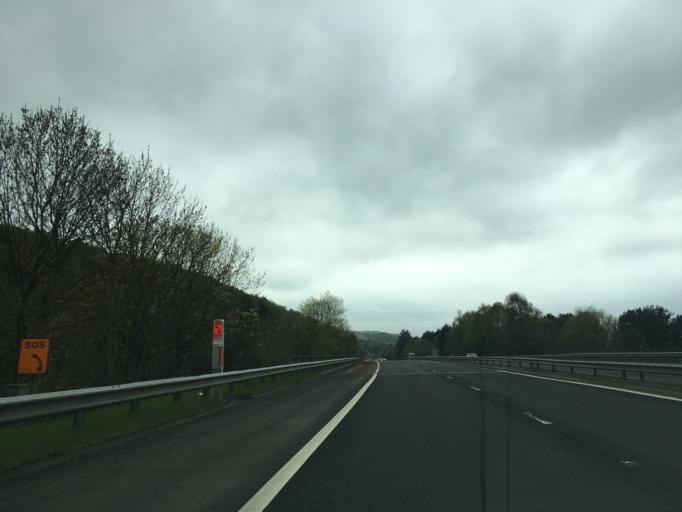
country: GB
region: Scotland
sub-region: West Dunbartonshire
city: Dumbarton
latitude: 55.9235
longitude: -4.5554
